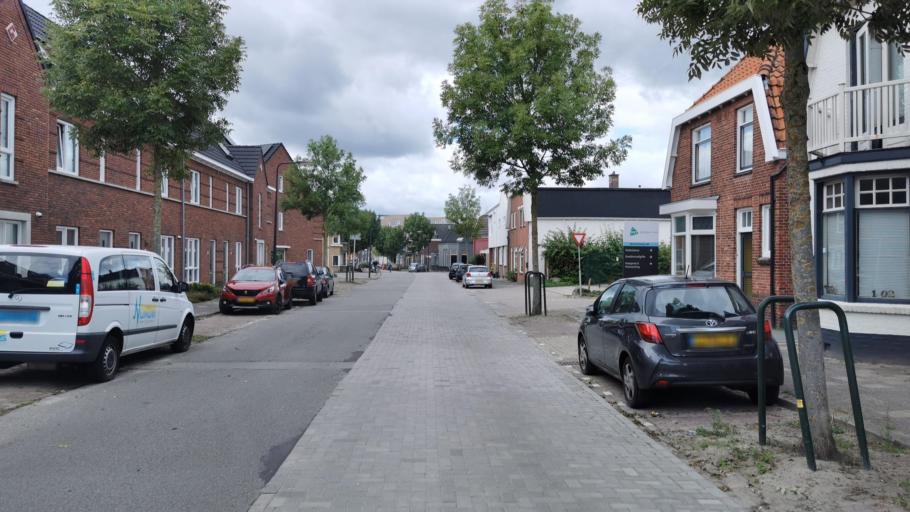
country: NL
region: Overijssel
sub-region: Gemeente Enschede
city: Enschede
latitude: 52.2142
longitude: 6.8917
